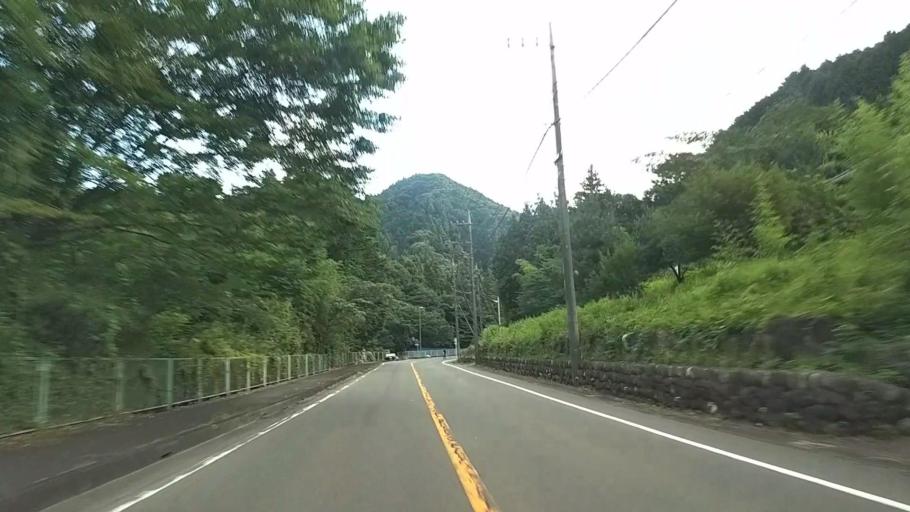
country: JP
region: Tokyo
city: Hachioji
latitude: 35.5587
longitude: 139.2355
